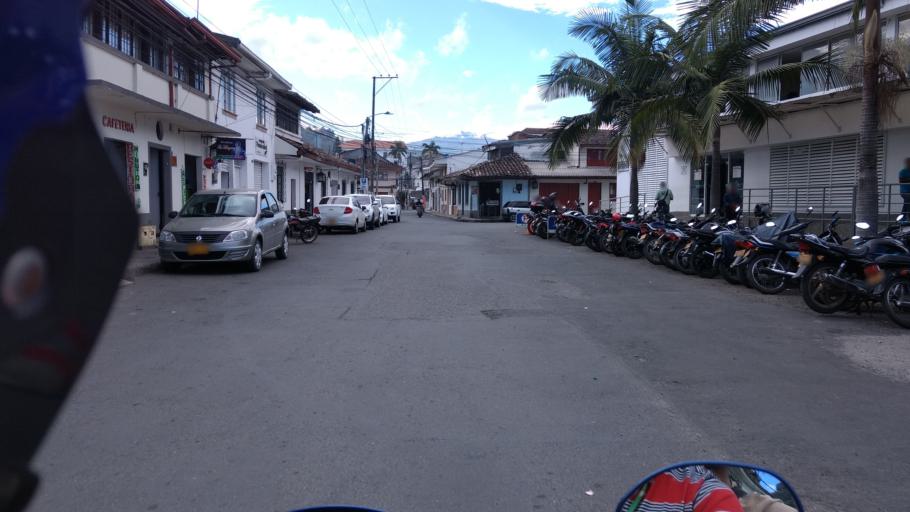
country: CO
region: Cauca
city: Popayan
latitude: 2.4451
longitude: -76.6086
